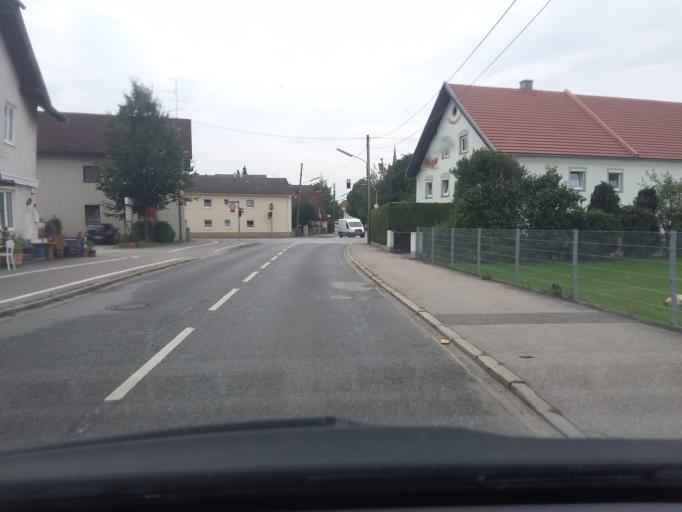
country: DE
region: Bavaria
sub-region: Upper Bavaria
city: Oberschleissheim
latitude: 48.2184
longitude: 11.5302
